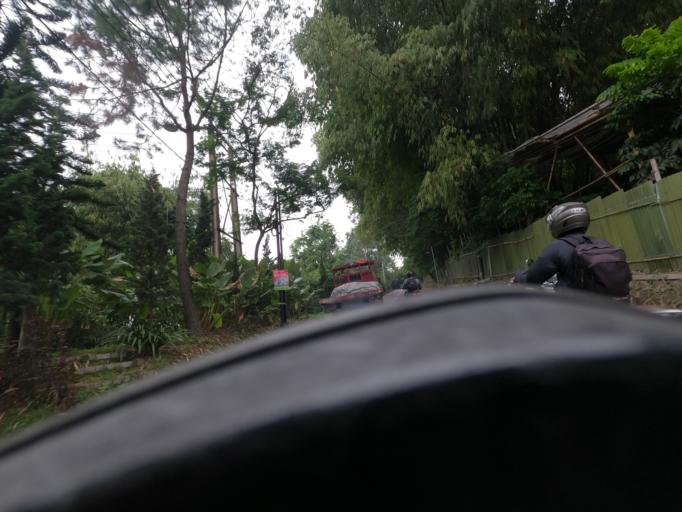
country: ID
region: West Java
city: Lembang
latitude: -6.7984
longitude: 107.5777
